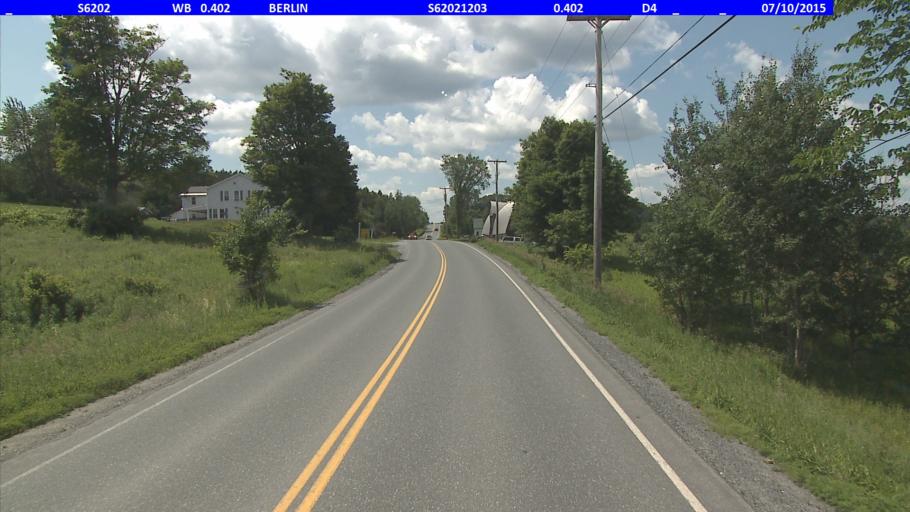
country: US
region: Vermont
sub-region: Washington County
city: South Barre
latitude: 44.1912
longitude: -72.5481
